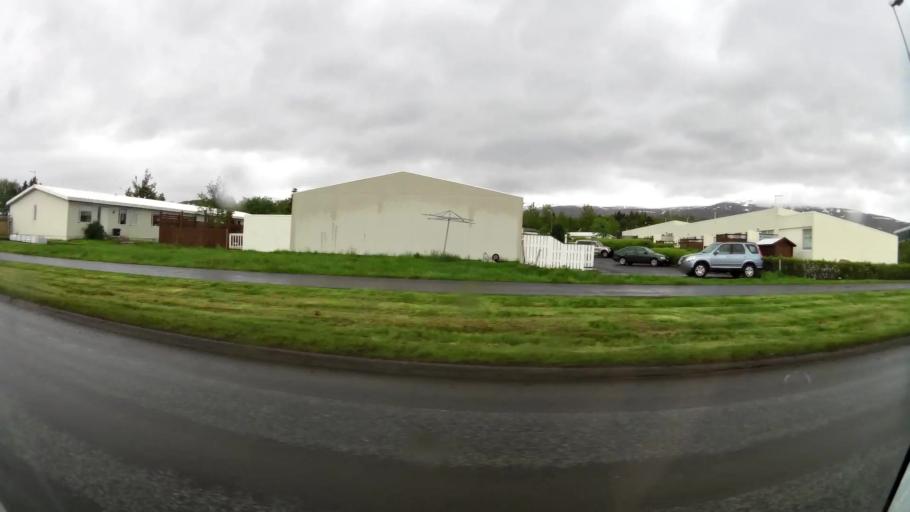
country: IS
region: Northeast
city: Akureyri
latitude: 65.6965
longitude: -18.1144
